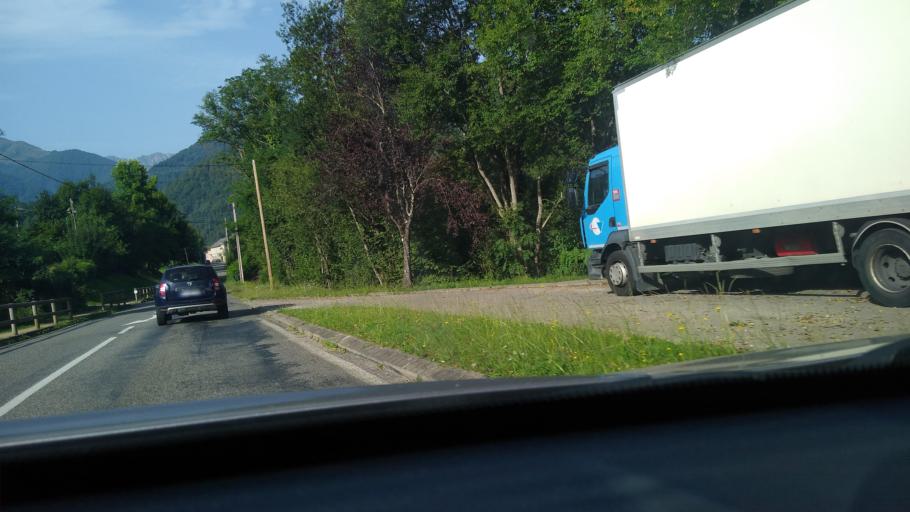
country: FR
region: Midi-Pyrenees
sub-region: Departement de l'Ariege
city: Saint-Girons
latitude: 42.8677
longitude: 1.2079
